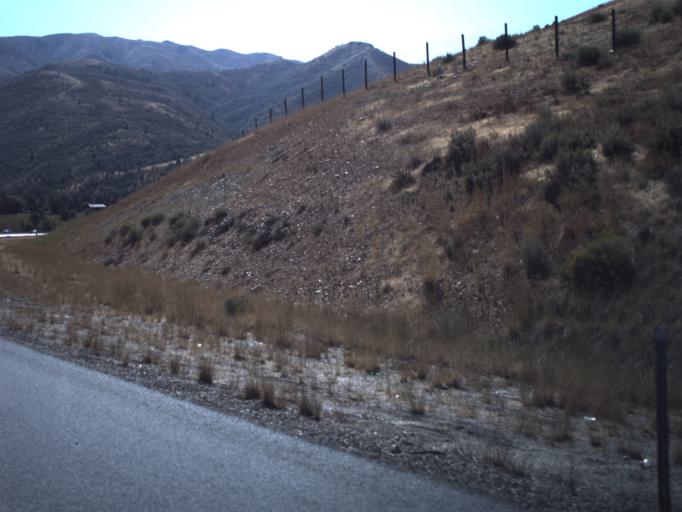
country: US
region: Utah
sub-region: Box Elder County
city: Brigham City
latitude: 41.5033
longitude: -111.9459
